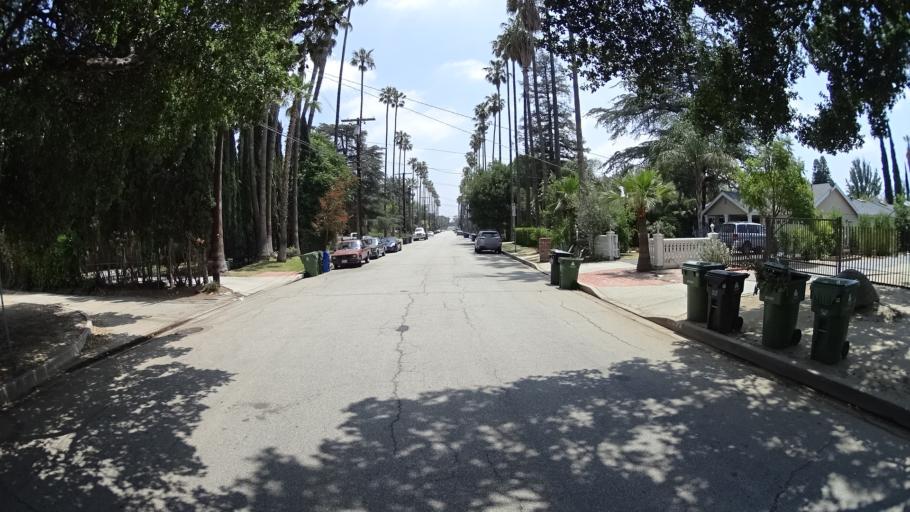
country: US
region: California
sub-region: Los Angeles County
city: Van Nuys
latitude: 34.1886
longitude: -118.4620
